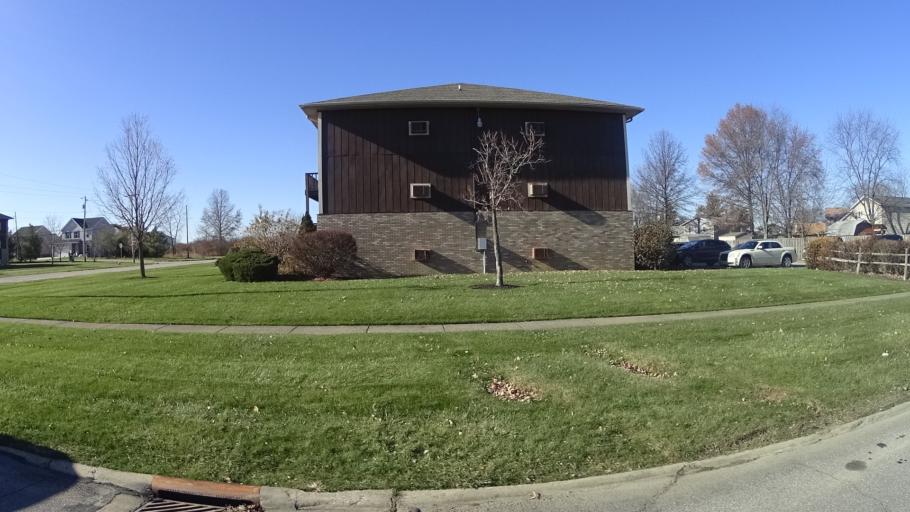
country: US
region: Ohio
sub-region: Lorain County
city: Elyria
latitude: 41.3655
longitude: -82.1645
